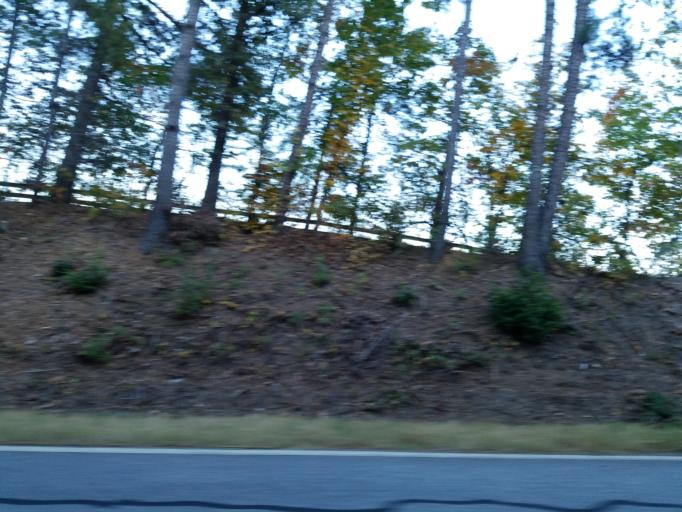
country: US
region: Georgia
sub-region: Lumpkin County
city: Dahlonega
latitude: 34.5322
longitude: -84.0582
